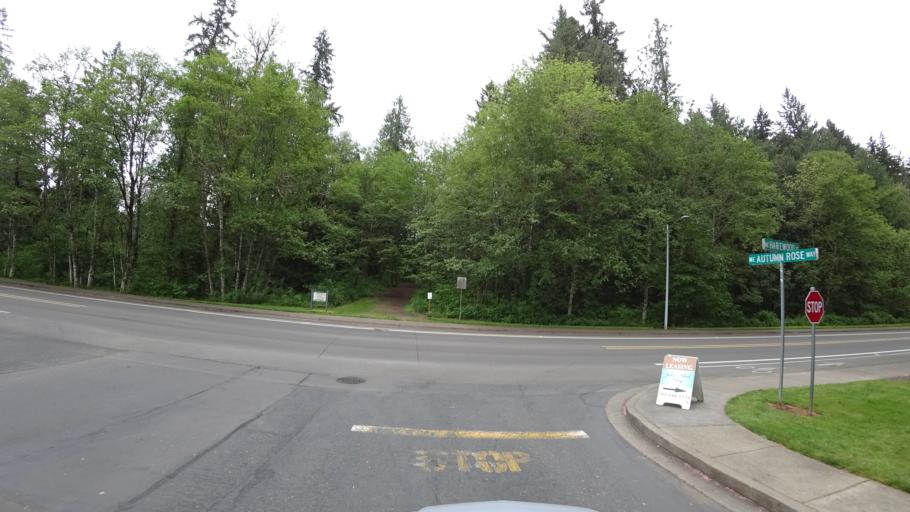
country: US
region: Oregon
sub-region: Washington County
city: Hillsboro
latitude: 45.5376
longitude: -122.9882
